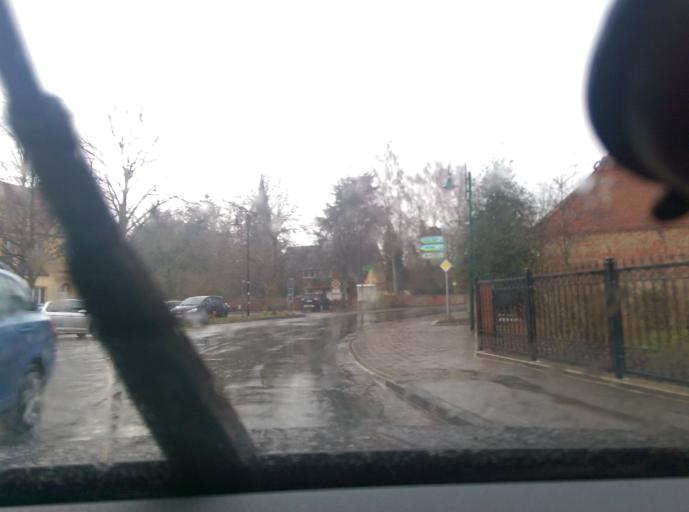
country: DE
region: Lower Saxony
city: Schwarmstedt
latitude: 52.6776
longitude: 9.6164
